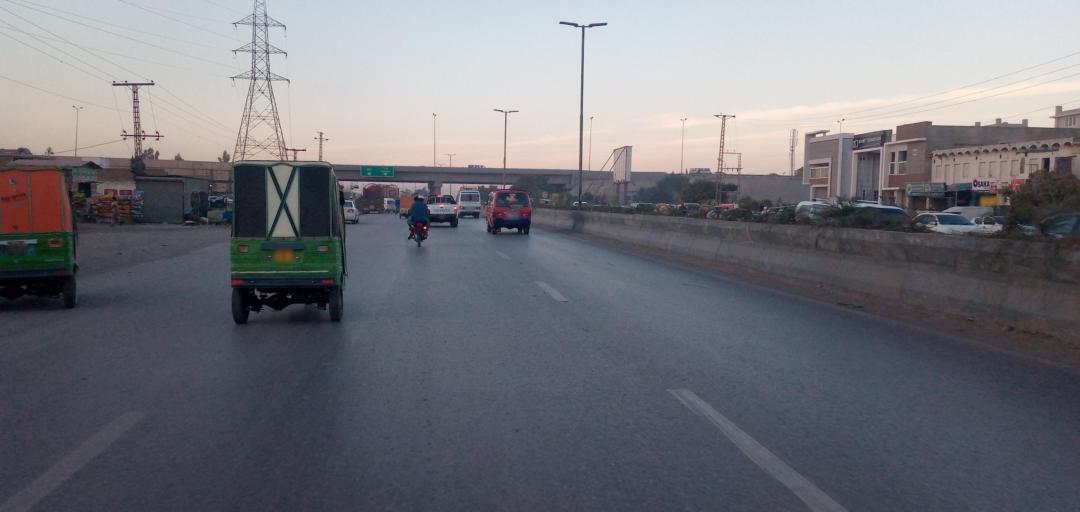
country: PK
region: Khyber Pakhtunkhwa
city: Peshawar
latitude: 34.0220
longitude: 71.6214
